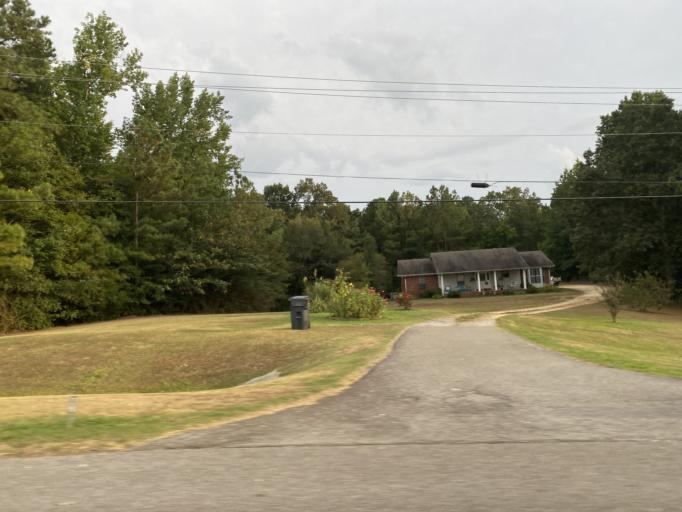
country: US
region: Alabama
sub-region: Franklin County
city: Red Bay
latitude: 34.4492
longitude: -88.0656
